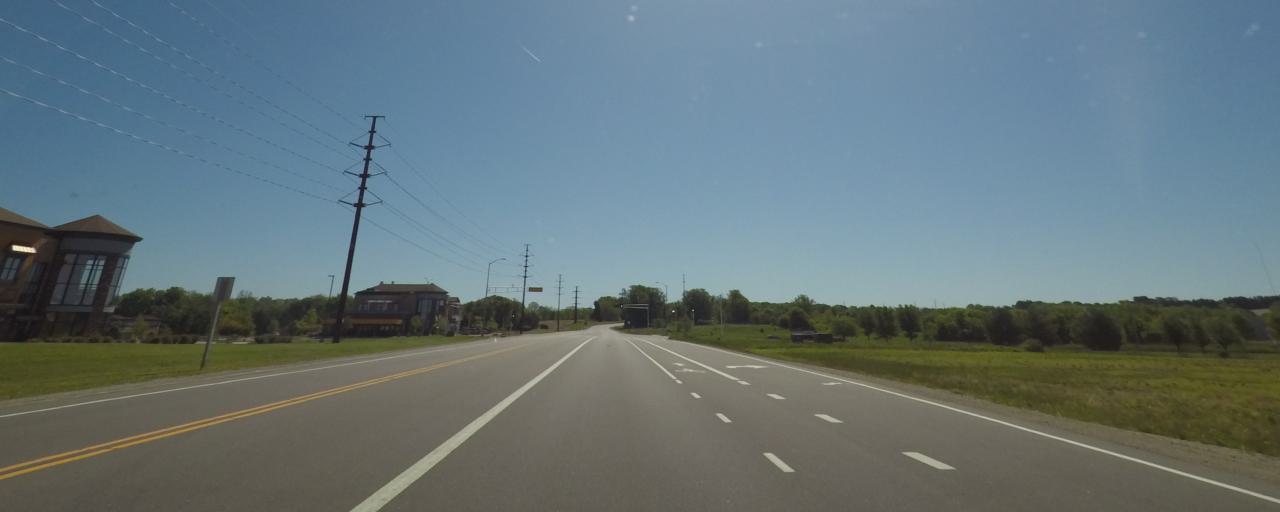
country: US
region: Wisconsin
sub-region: Dane County
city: Verona
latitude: 42.9723
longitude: -89.5086
